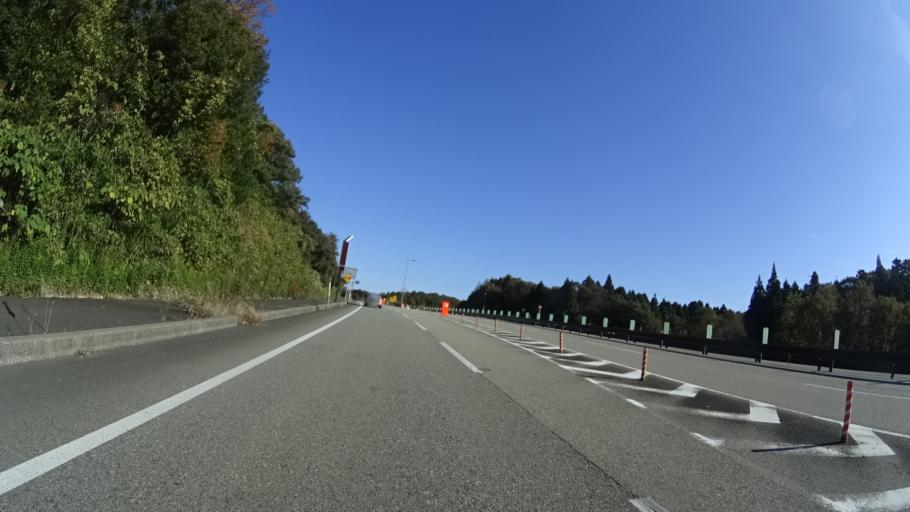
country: JP
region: Ishikawa
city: Komatsu
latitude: 36.3870
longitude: 136.4915
